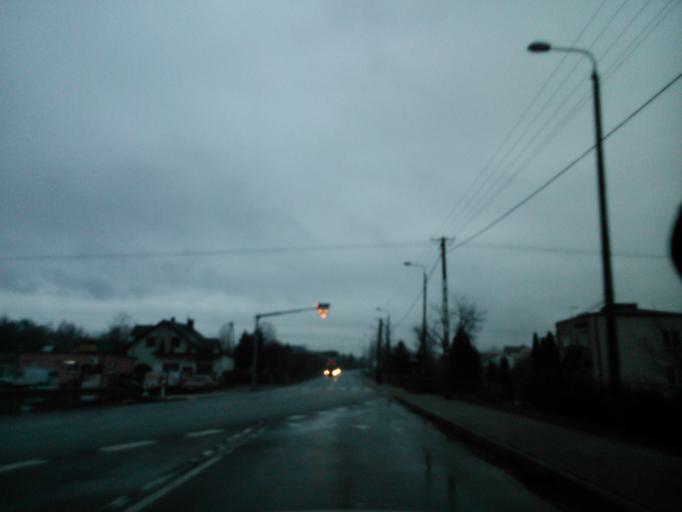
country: PL
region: Lublin Voivodeship
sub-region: Powiat krasnicki
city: Krasnik
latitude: 50.9040
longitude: 22.2726
